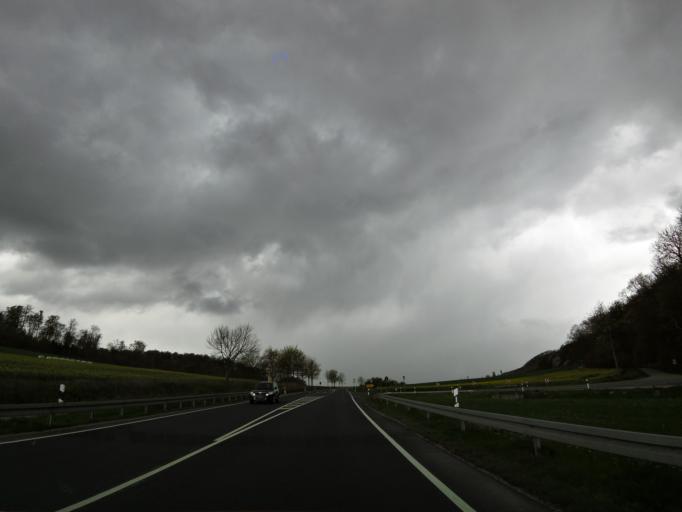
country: DE
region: Lower Saxony
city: Hahausen
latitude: 51.9503
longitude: 10.2050
